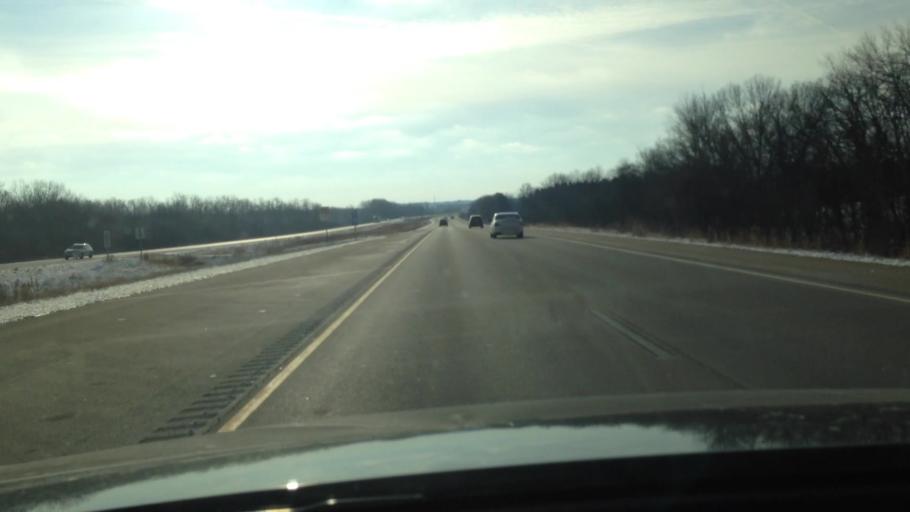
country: US
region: Wisconsin
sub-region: Waukesha County
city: Mukwonago
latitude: 42.8731
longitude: -88.2900
